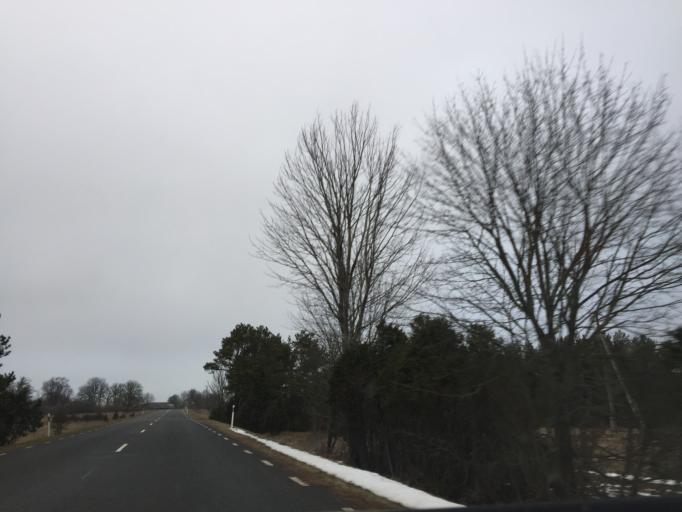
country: EE
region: Saare
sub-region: Kuressaare linn
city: Kuressaare
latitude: 58.5575
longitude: 22.3150
